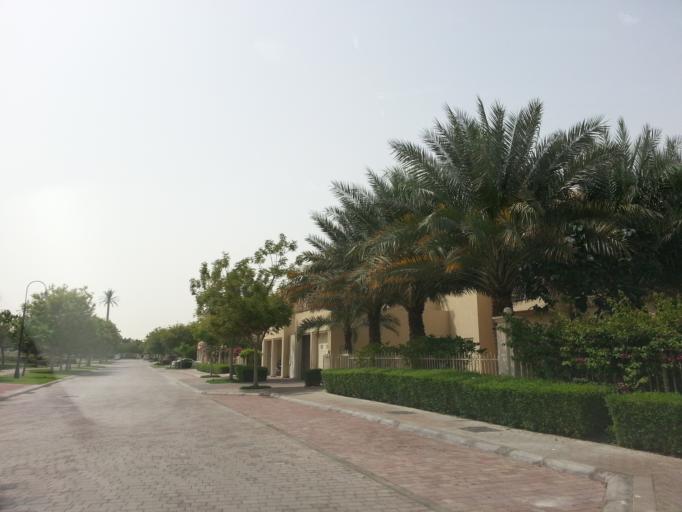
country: AE
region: Dubai
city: Dubai
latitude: 25.0367
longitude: 55.2140
